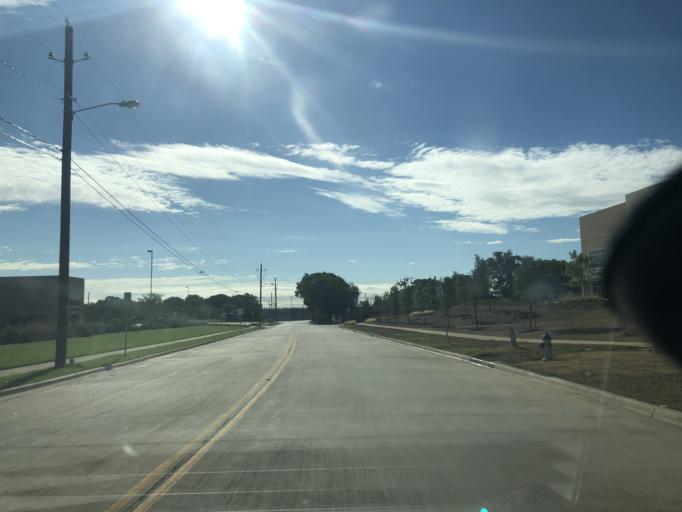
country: US
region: Texas
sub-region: Tarrant County
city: Euless
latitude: 32.8221
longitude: -97.0328
